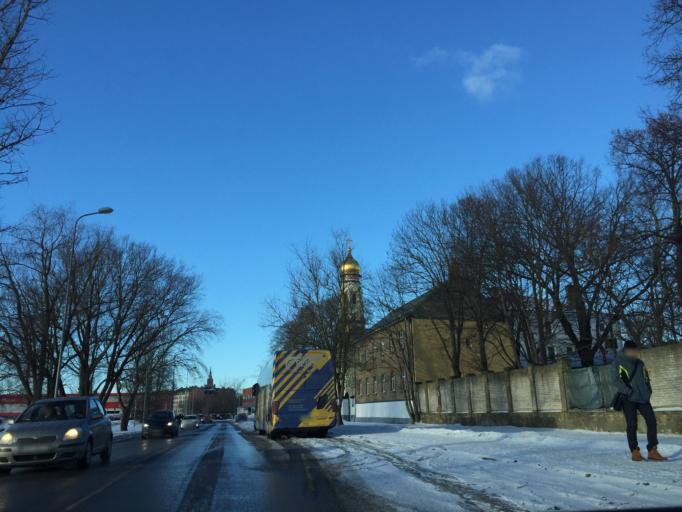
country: LV
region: Riga
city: Riga
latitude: 56.9366
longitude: 24.1411
